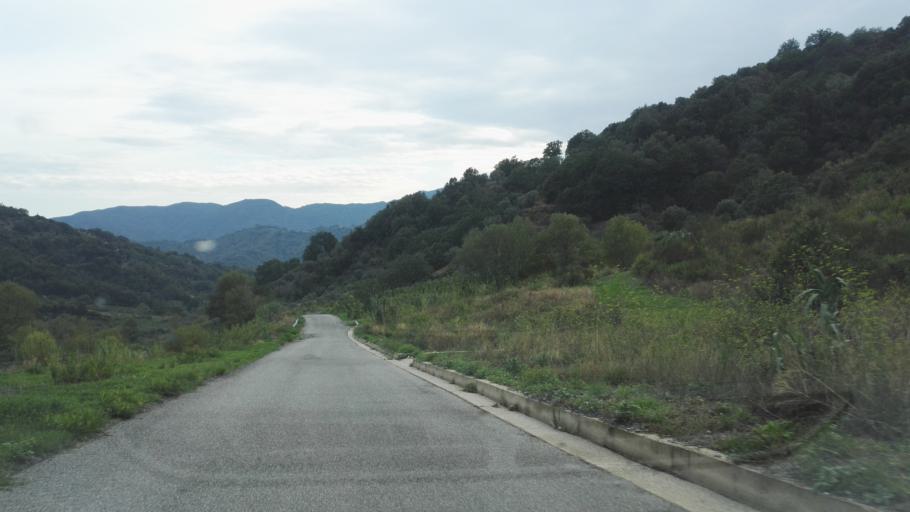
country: IT
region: Calabria
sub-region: Provincia di Reggio Calabria
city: Caulonia
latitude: 38.4328
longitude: 16.3953
